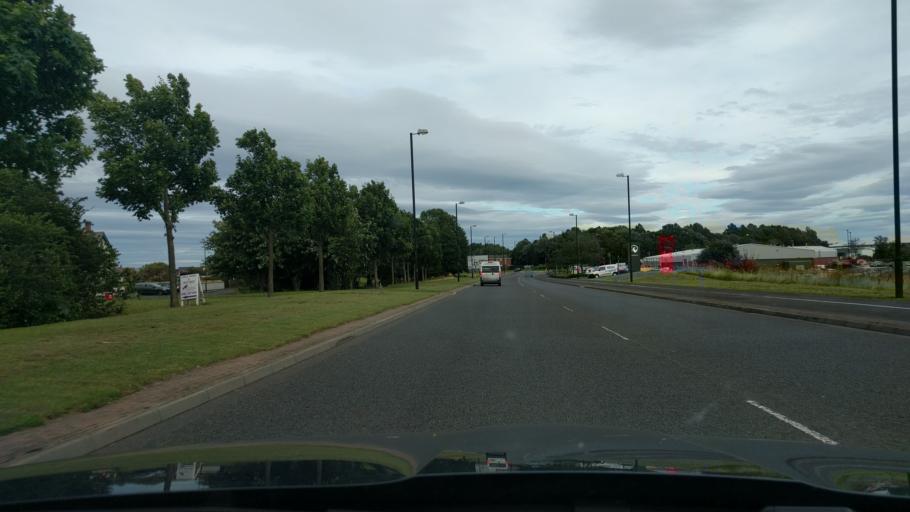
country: GB
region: England
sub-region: Borough of North Tyneside
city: Shiremoor
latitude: 55.0256
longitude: -1.4969
